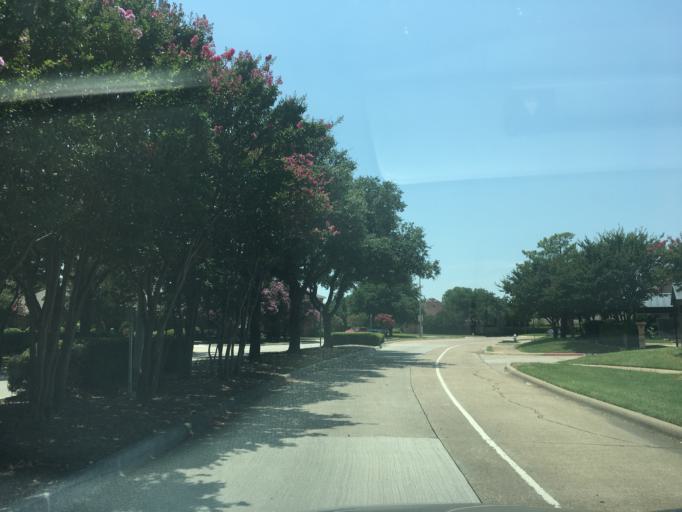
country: US
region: Texas
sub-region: Dallas County
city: Carrollton
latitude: 32.9489
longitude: -96.8600
